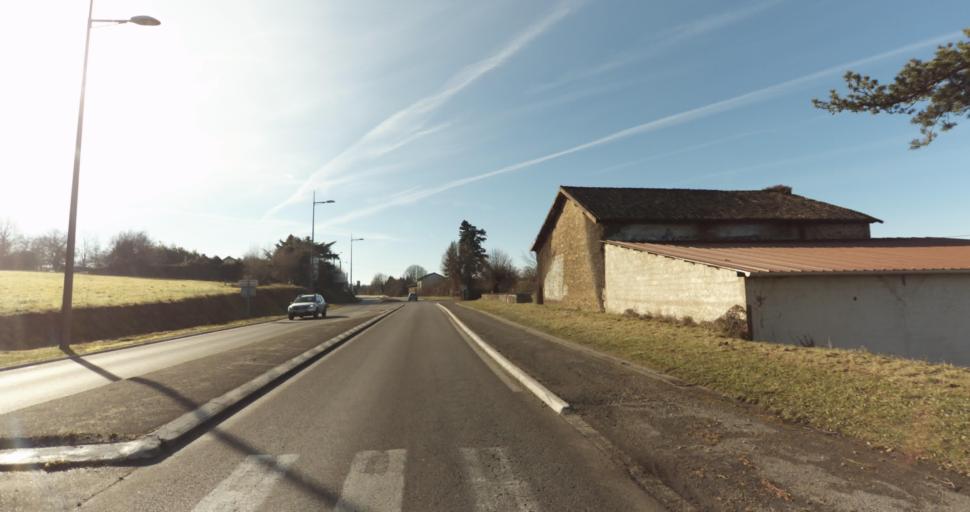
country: FR
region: Limousin
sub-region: Departement de la Haute-Vienne
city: Aixe-sur-Vienne
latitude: 45.7947
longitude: 1.1148
